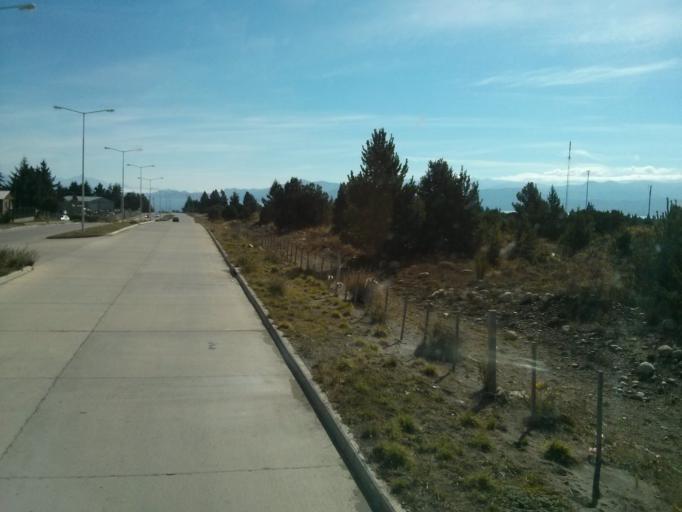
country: AR
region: Rio Negro
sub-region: Departamento de Bariloche
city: San Carlos de Bariloche
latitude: -41.1402
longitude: -71.2751
